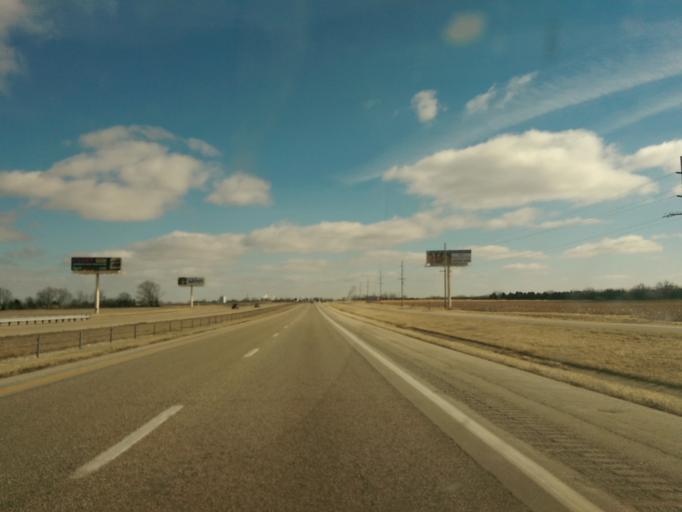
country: US
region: Missouri
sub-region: Montgomery County
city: Montgomery City
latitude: 38.8863
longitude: -91.4095
